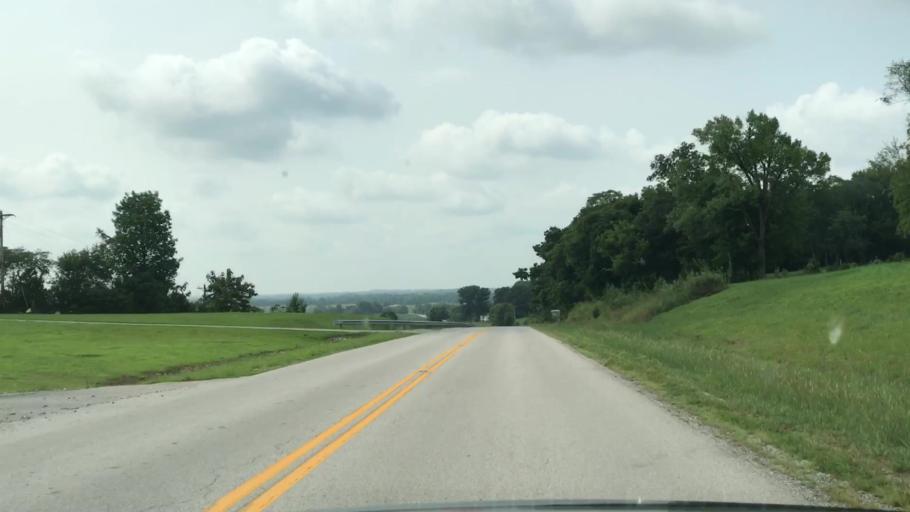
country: US
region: Kentucky
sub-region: Edmonson County
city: Brownsville
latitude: 37.1050
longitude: -86.1462
